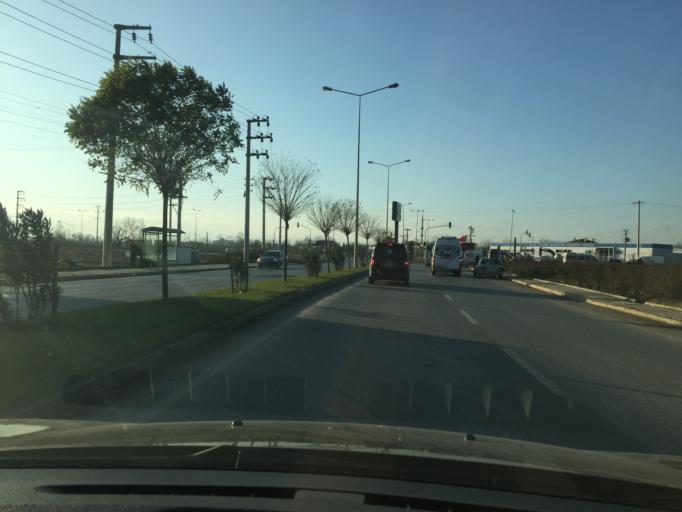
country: TR
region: Sakarya
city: Sogutlu
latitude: 40.9051
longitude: 30.4863
